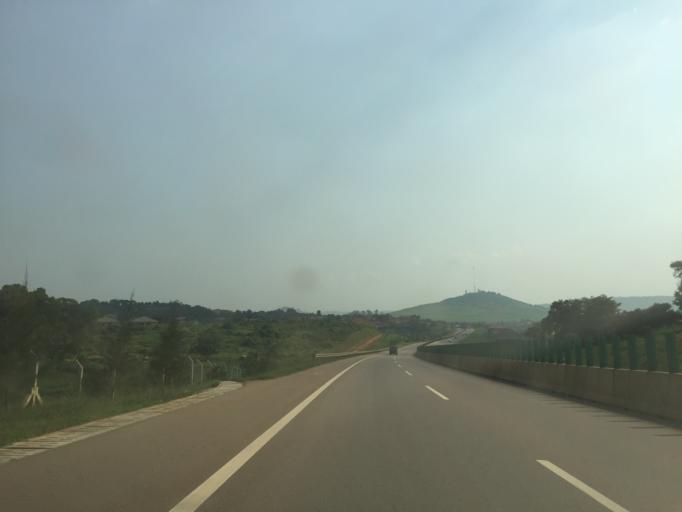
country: UG
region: Central Region
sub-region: Wakiso District
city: Kajansi
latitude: 0.2419
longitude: 32.5240
